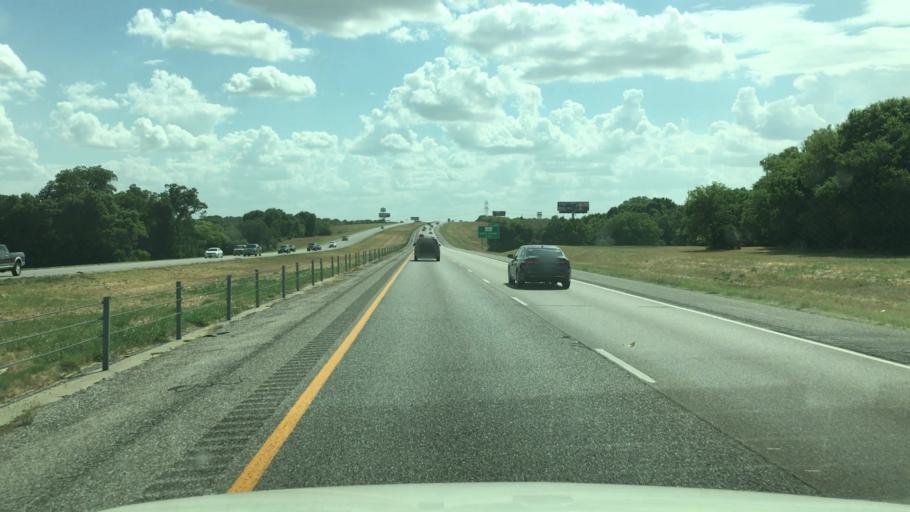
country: US
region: Texas
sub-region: Ellis County
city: Plum Grove
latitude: 32.0890
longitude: -97.0350
